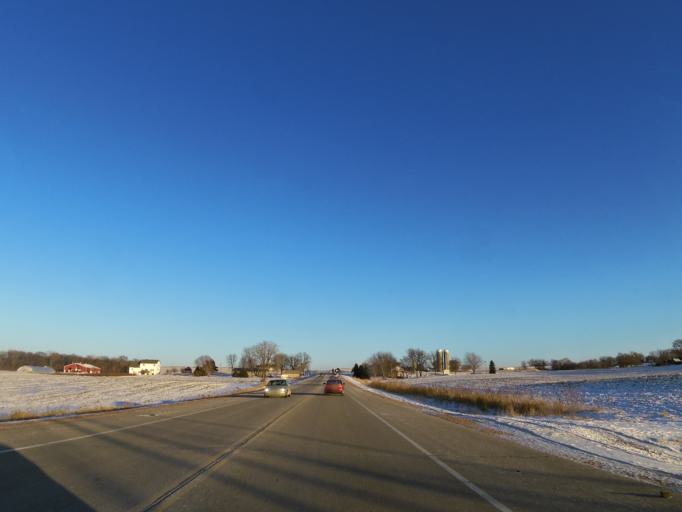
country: US
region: Minnesota
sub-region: Carver County
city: Chaska
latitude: 44.7619
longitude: -93.5661
